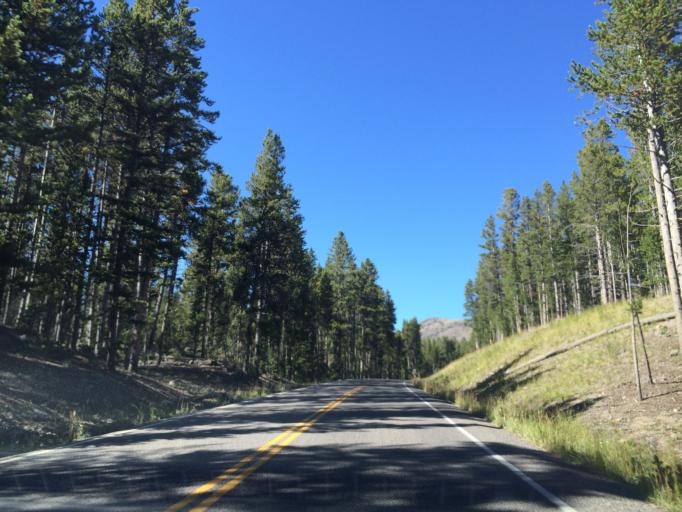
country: US
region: Montana
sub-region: Gallatin County
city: West Yellowstone
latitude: 44.7430
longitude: -110.4943
